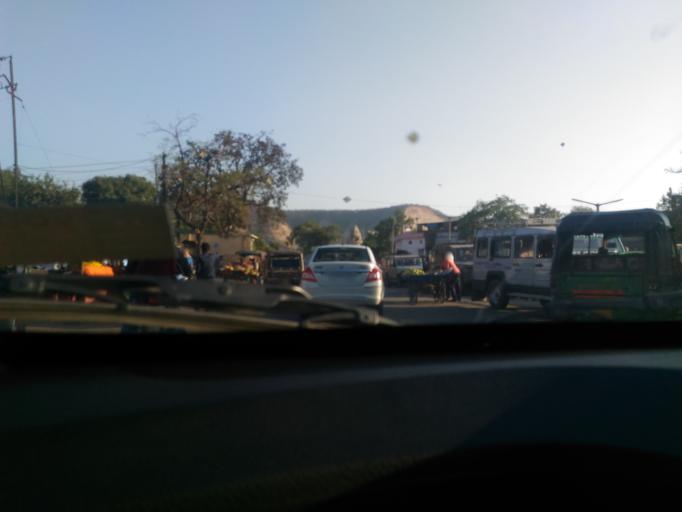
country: IN
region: Rajasthan
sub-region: Jaipur
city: Jaipur
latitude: 26.9041
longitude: 75.8448
